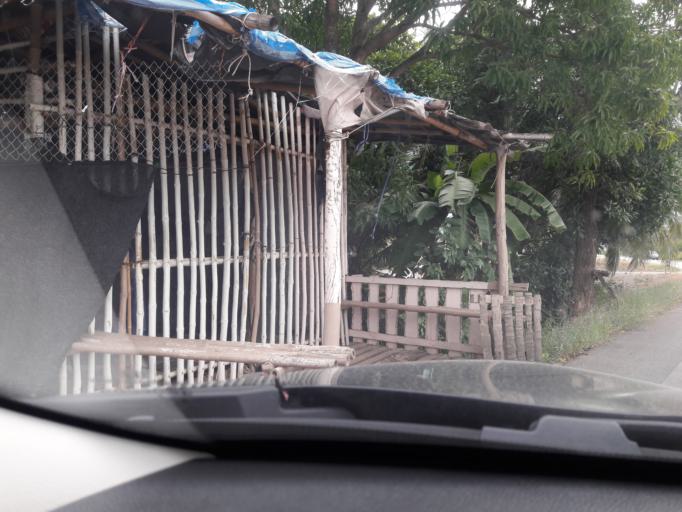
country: TH
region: Ratchaburi
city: Damnoen Saduak
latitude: 13.5932
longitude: 99.9387
